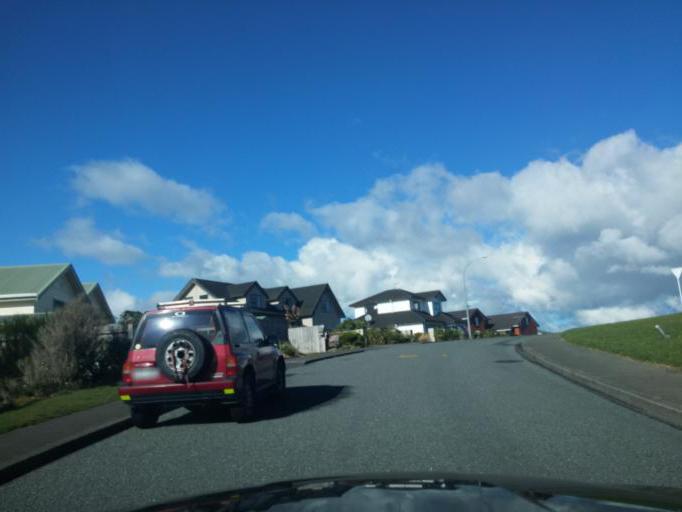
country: NZ
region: Wellington
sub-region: Wellington City
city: Wellington
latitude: -41.2354
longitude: 174.7930
